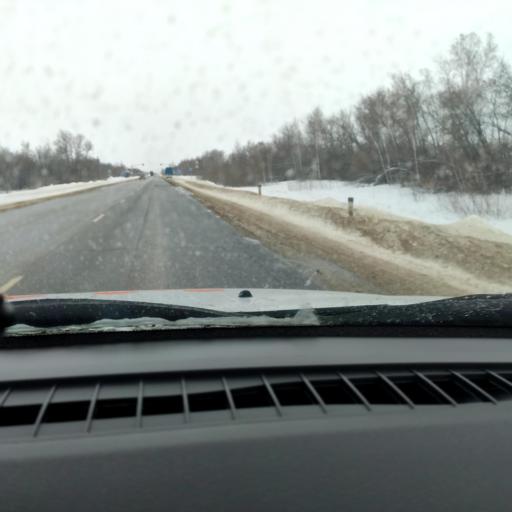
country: RU
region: Samara
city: Dubovyy Umet
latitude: 52.8766
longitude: 50.4337
